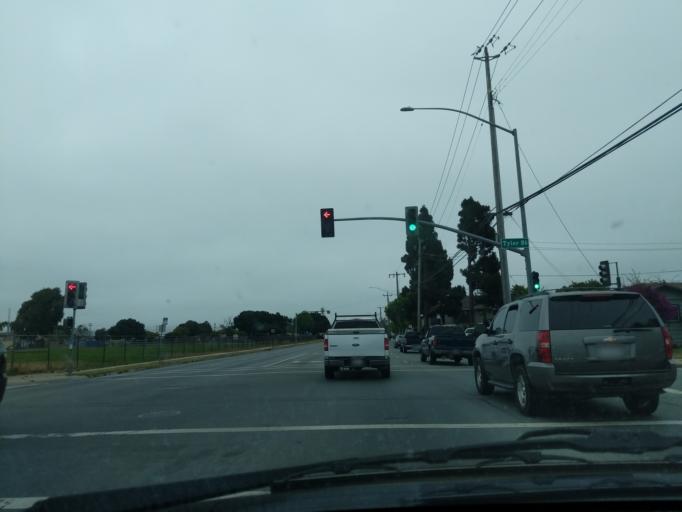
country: US
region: California
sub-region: Monterey County
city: Boronda
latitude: 36.6983
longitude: -121.6597
